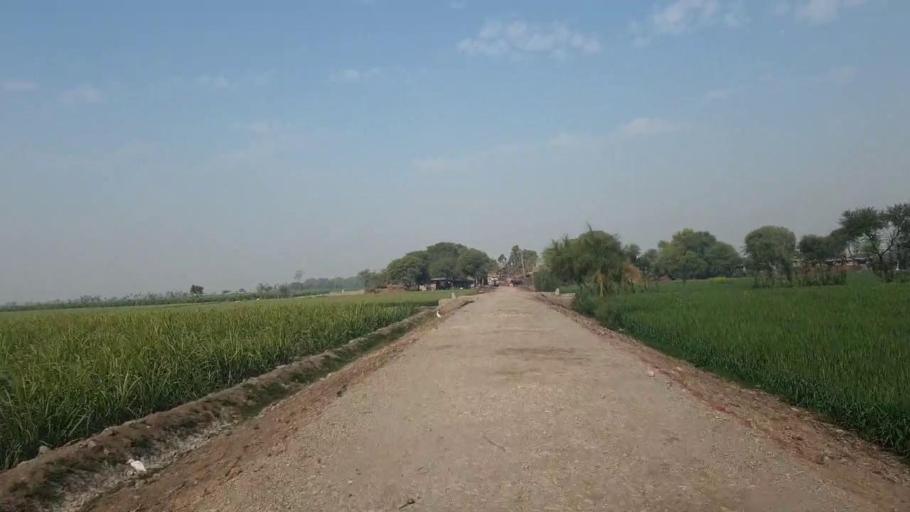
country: PK
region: Sindh
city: Tando Allahyar
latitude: 25.3805
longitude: 68.7659
